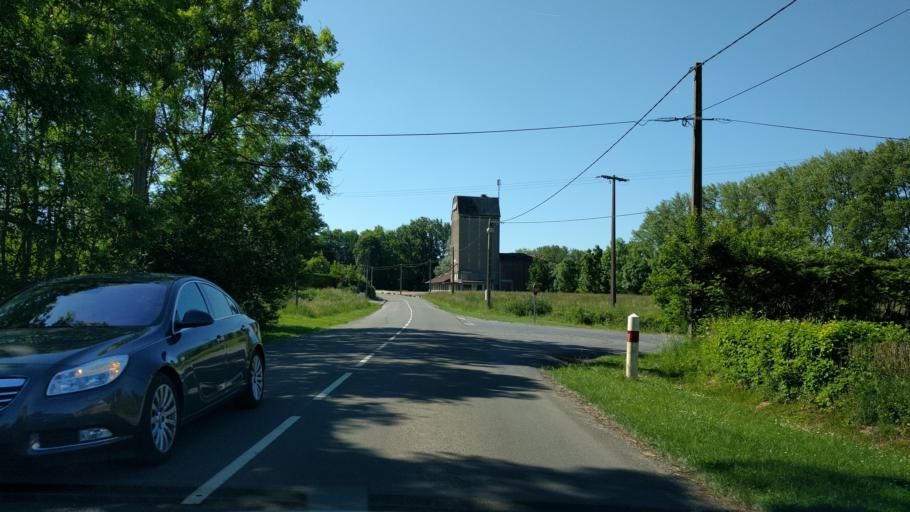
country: FR
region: Picardie
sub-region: Departement de la Somme
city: Peronne
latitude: 49.9198
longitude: 2.9212
